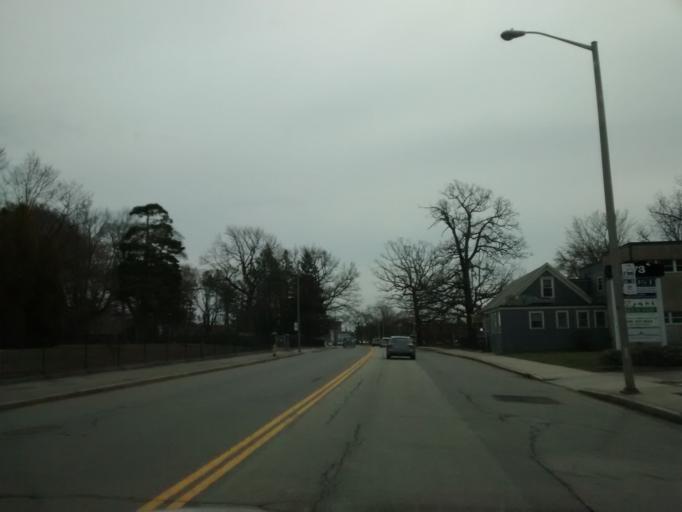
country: US
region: Massachusetts
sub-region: Worcester County
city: Worcester
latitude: 42.2798
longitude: -71.8048
